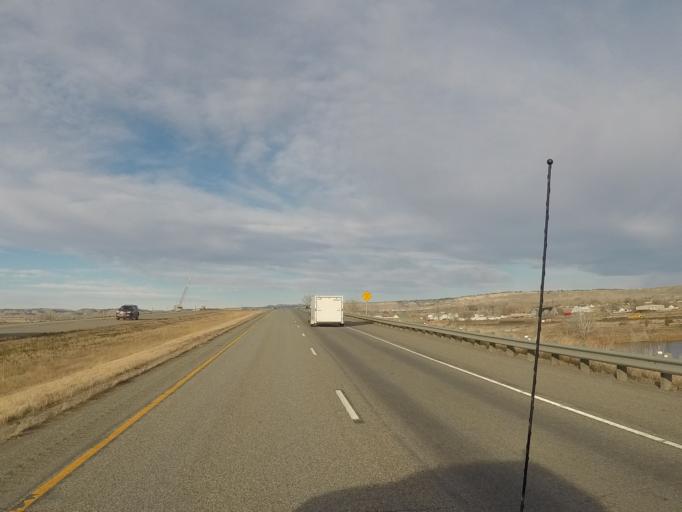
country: US
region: Montana
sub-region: Yellowstone County
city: Laurel
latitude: 45.6624
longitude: -108.7857
